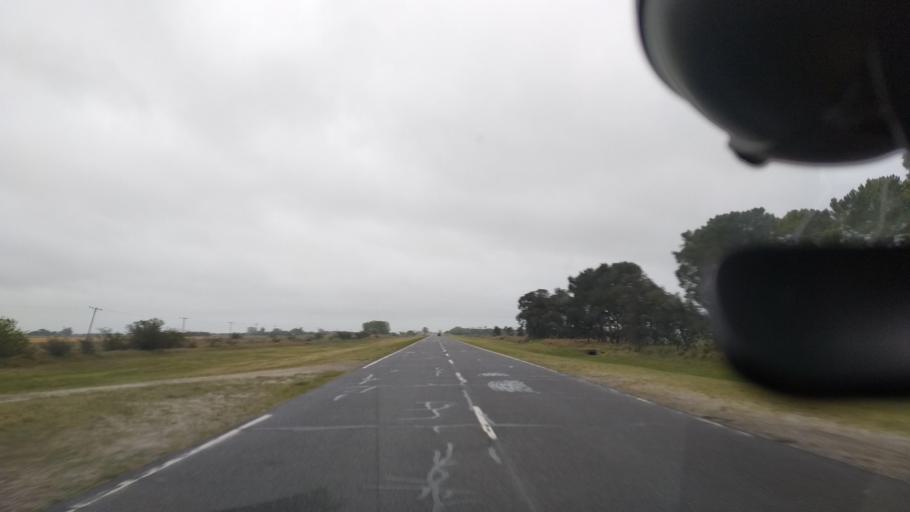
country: AR
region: Buenos Aires
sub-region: Partido de Dolores
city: Dolores
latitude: -36.0469
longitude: -57.4451
